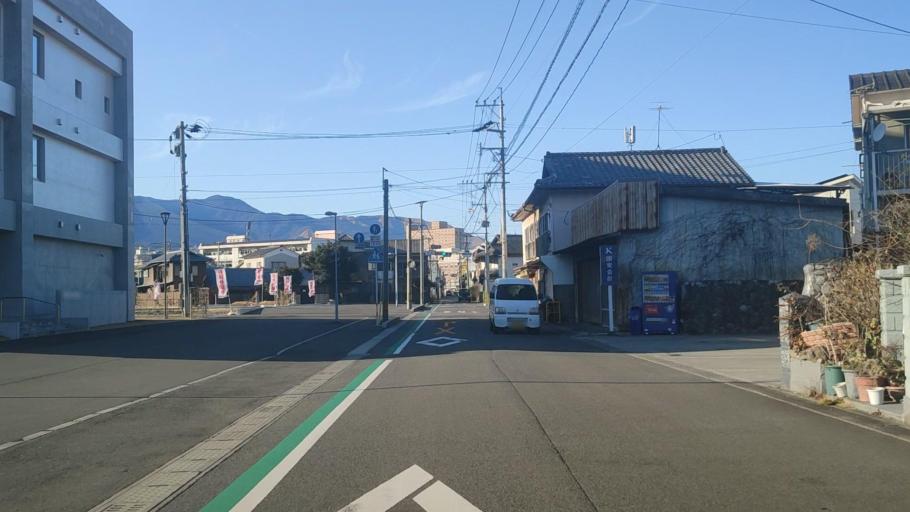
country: JP
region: Oita
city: Beppu
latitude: 33.2708
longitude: 131.5057
